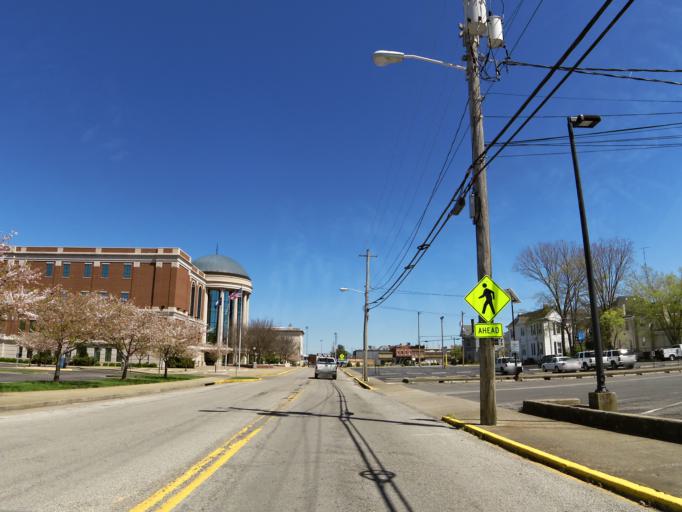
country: US
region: Kentucky
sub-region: Warren County
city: Bowling Green
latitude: 36.9933
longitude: -86.4450
